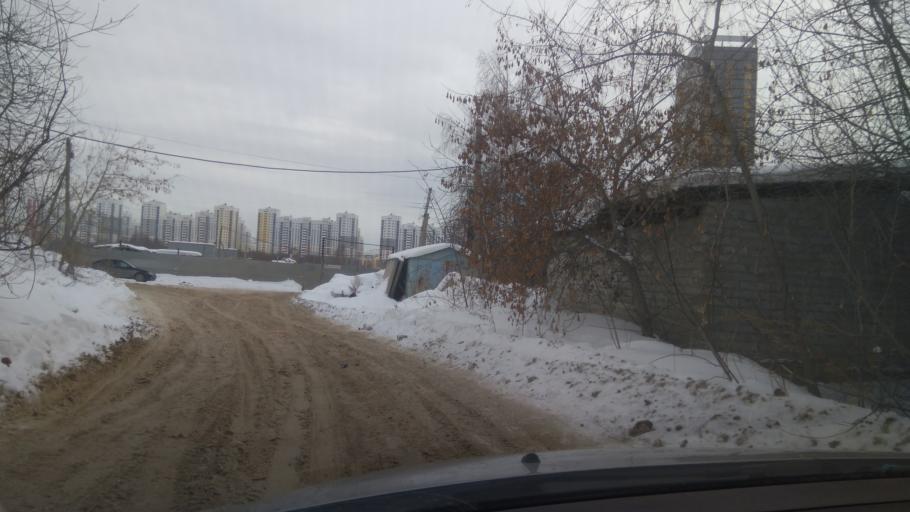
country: RU
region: Sverdlovsk
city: Shirokaya Rechka
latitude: 56.7990
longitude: 60.4973
